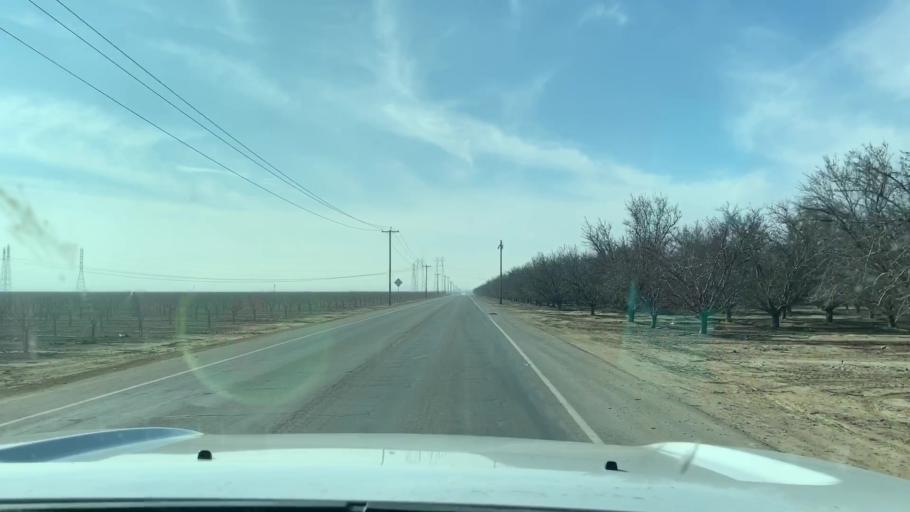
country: US
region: California
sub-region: Kern County
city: Buttonwillow
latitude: 35.4424
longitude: -119.4759
